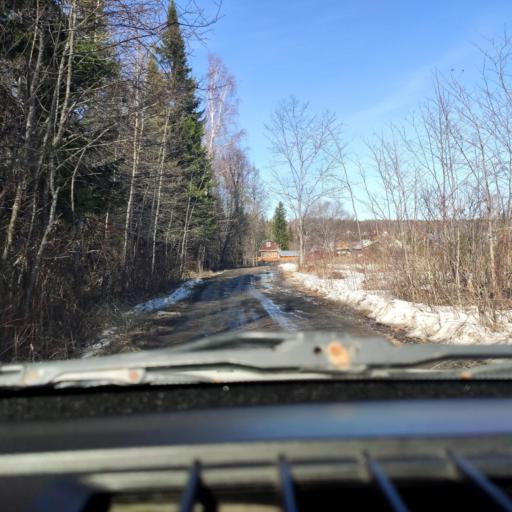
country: RU
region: Perm
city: Kultayevo
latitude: 57.8235
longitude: 55.7897
